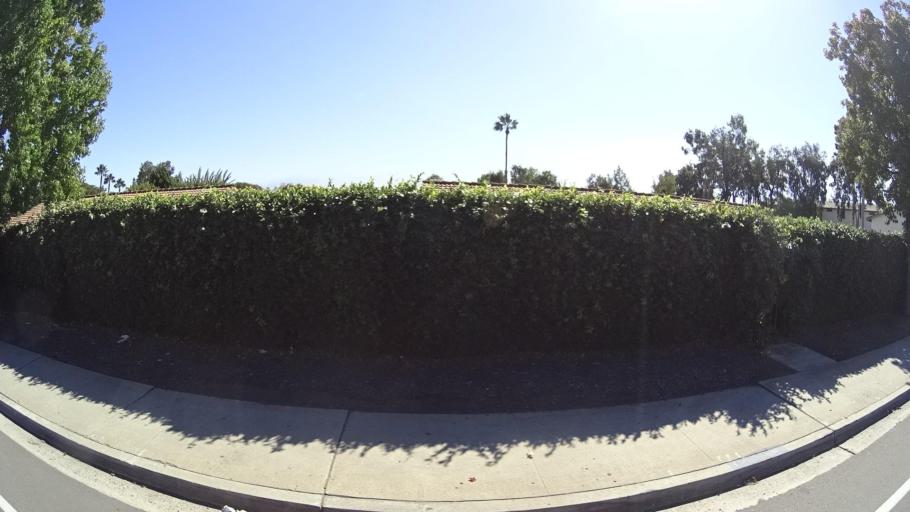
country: US
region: California
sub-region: San Diego County
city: La Presa
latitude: 32.6979
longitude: -117.0242
